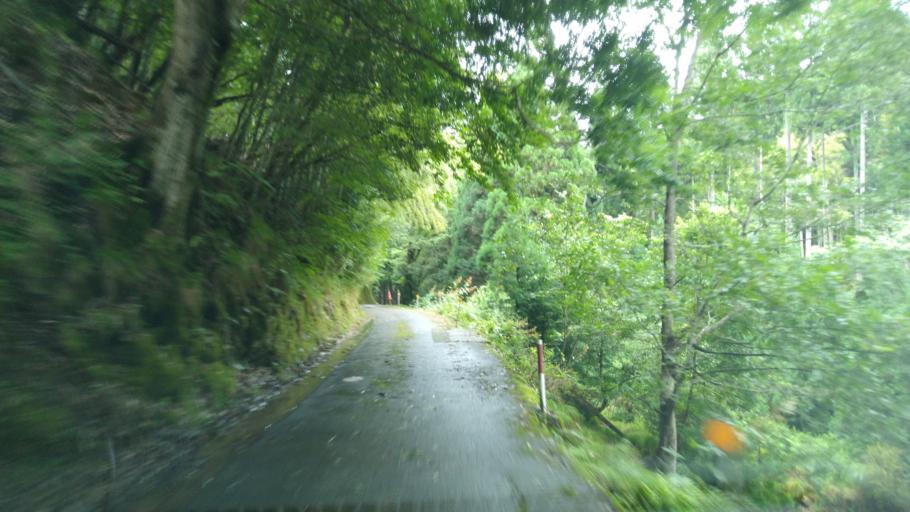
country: JP
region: Kyoto
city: Ayabe
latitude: 35.2331
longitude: 135.2675
